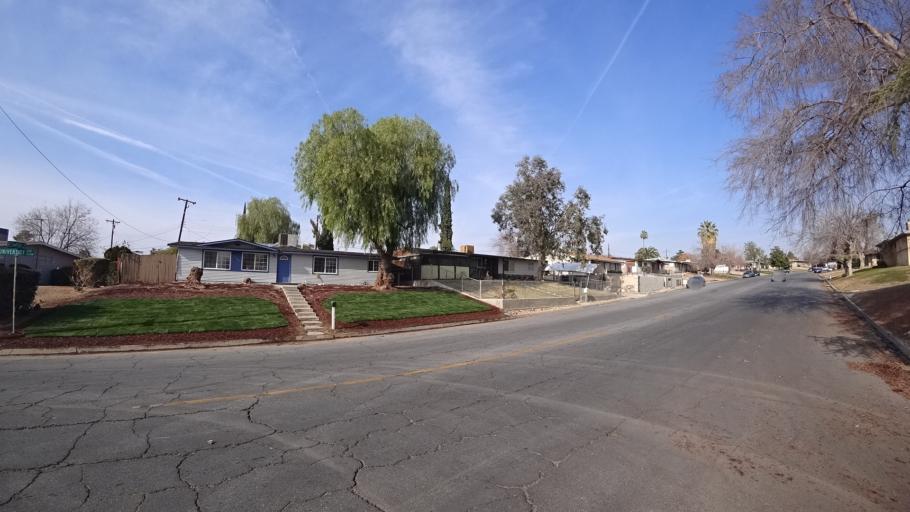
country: US
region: California
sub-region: Kern County
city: Oildale
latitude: 35.4026
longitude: -118.9804
